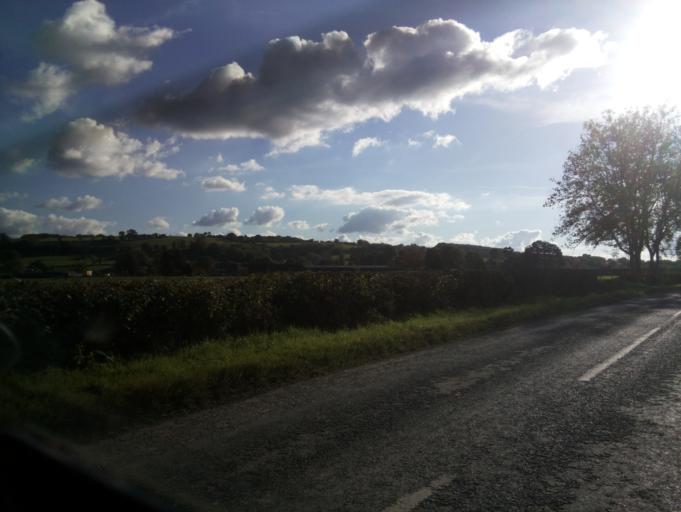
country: GB
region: England
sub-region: Herefordshire
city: Clifford
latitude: 52.1171
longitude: -3.0852
